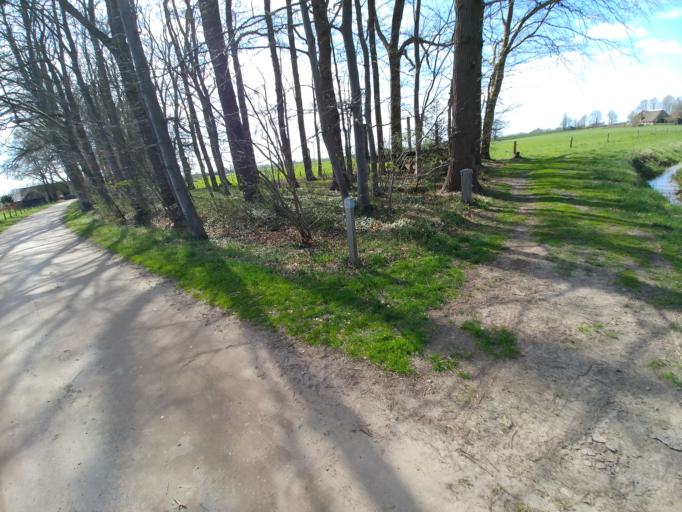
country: NL
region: Overijssel
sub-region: Gemeente Olst-Wijhe
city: Boskamp
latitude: 52.2981
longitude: 6.1231
